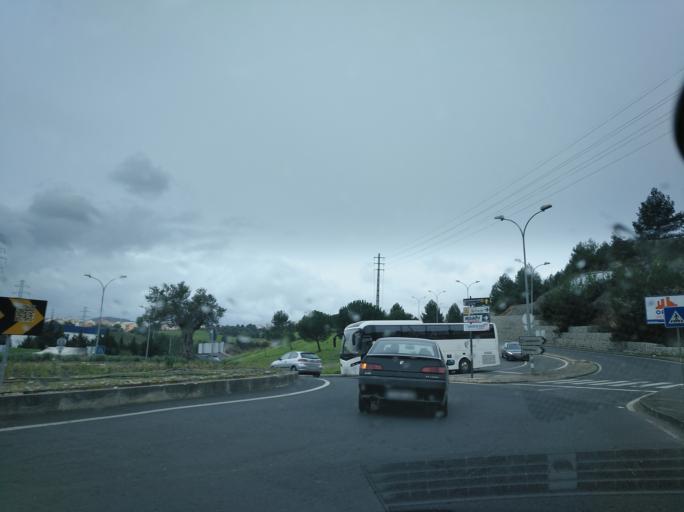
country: PT
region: Lisbon
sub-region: Odivelas
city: Odivelas
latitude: 38.7833
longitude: -9.1939
